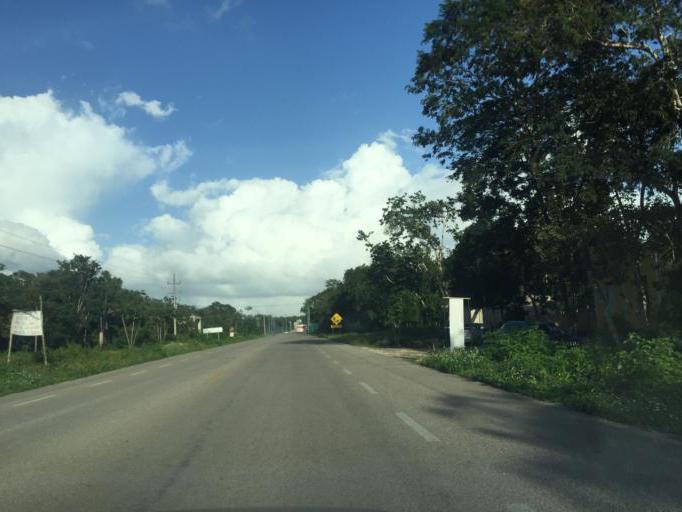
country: MX
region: Quintana Roo
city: Coba
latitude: 20.5064
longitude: -87.7217
